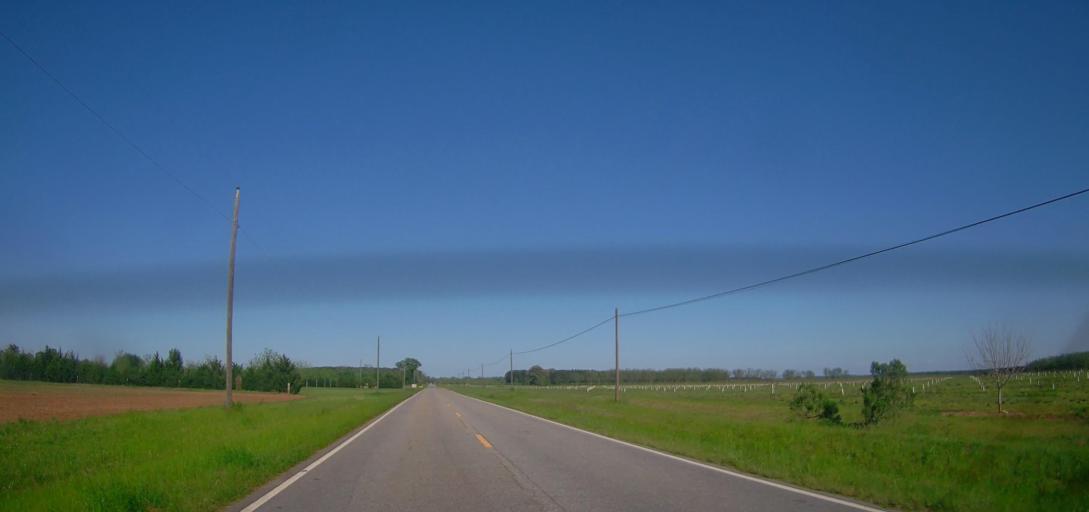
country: US
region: Georgia
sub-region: Houston County
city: Perry
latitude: 32.4515
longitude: -83.6636
